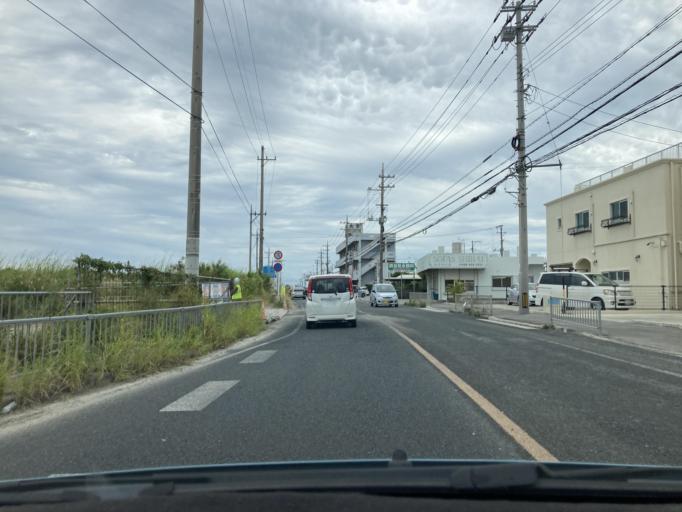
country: JP
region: Okinawa
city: Okinawa
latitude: 26.3828
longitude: 127.7435
